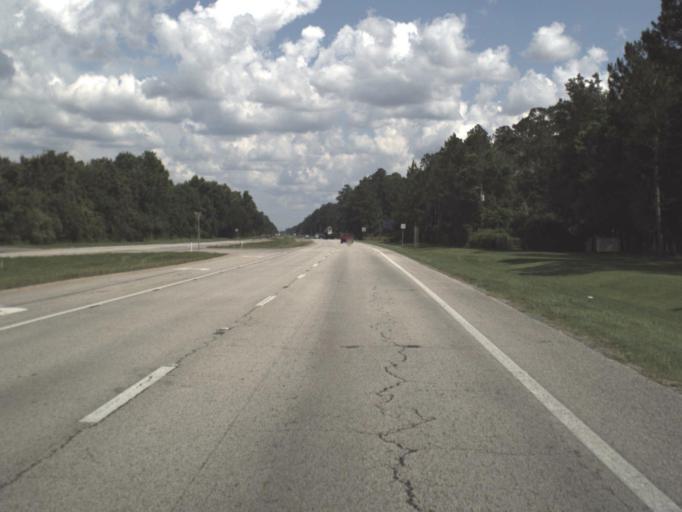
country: US
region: Florida
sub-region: Alachua County
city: Alachua
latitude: 29.7333
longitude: -82.3789
